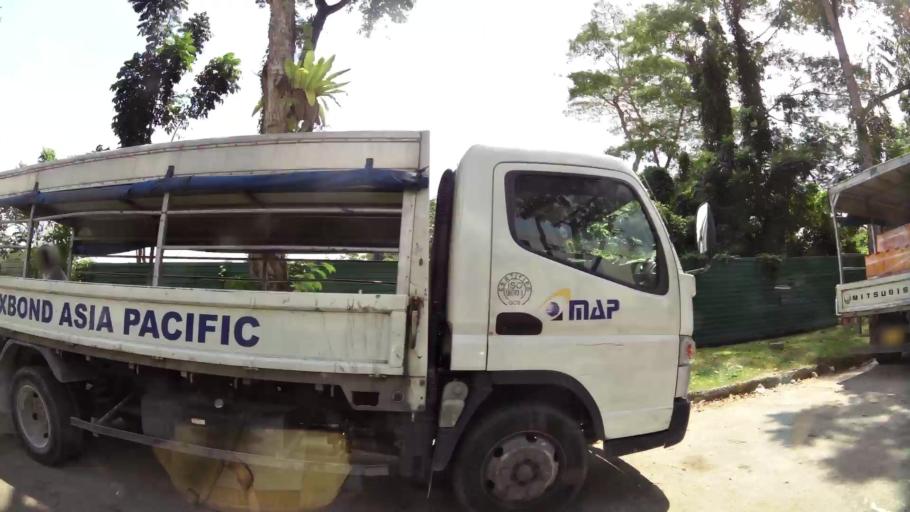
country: SG
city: Singapore
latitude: 1.3861
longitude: 103.8306
